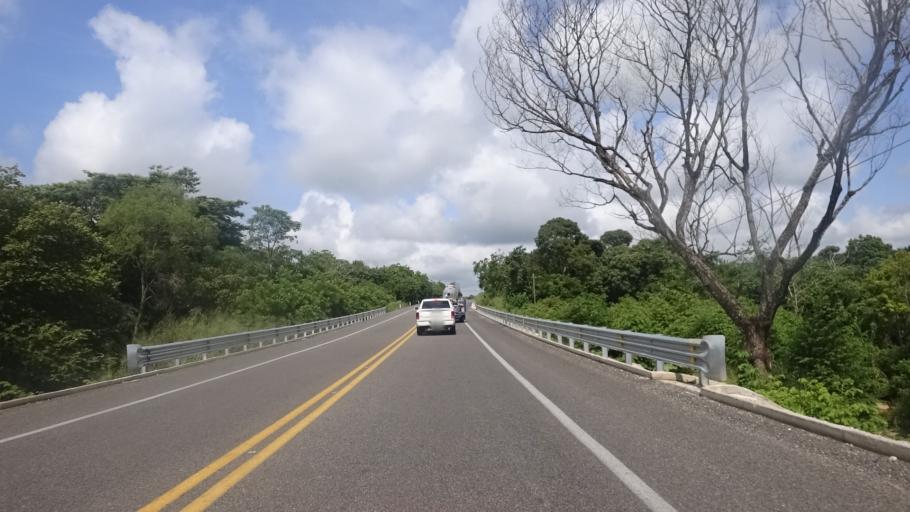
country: MX
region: Chiapas
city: Palenque
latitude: 17.5674
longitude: -92.0184
